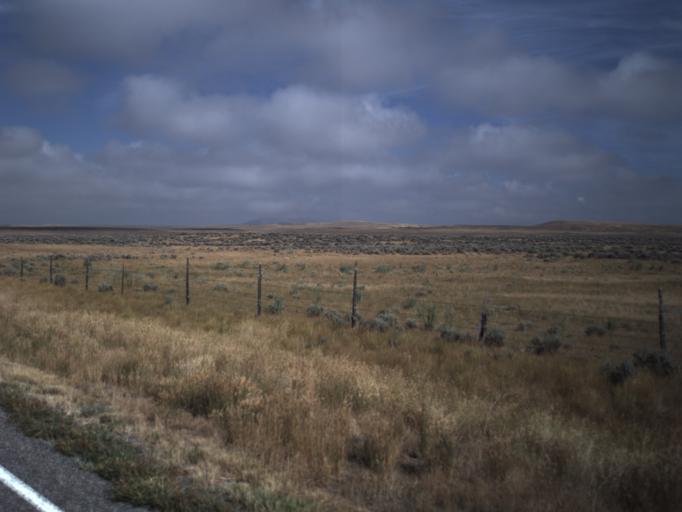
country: US
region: Wyoming
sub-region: Uinta County
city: Evanston
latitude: 41.4521
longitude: -111.0880
